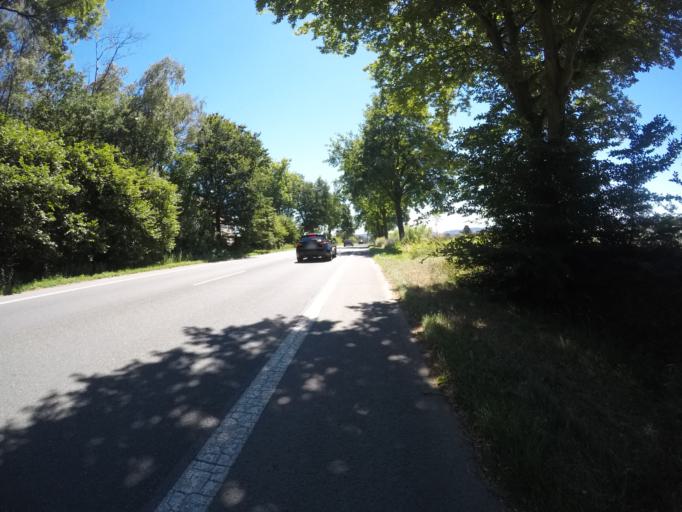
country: DE
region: North Rhine-Westphalia
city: Enger
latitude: 52.0792
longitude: 8.5839
